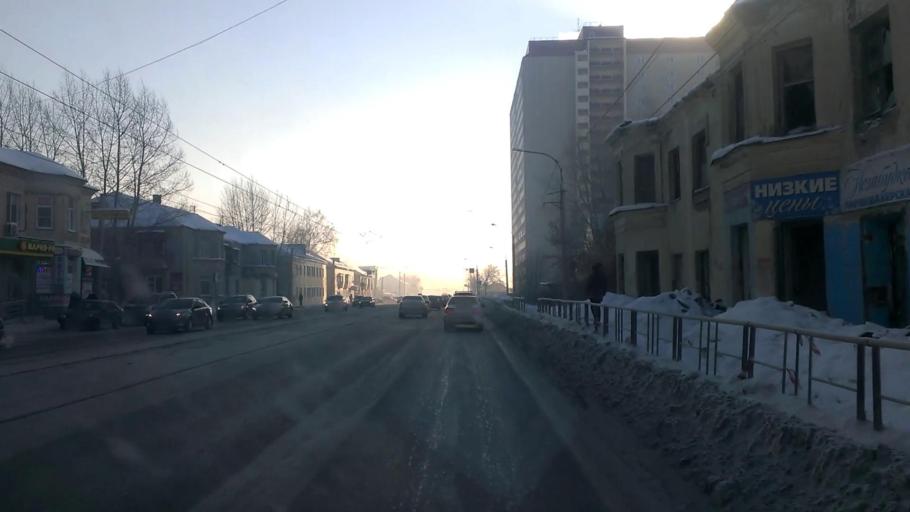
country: RU
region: Altai Krai
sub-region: Gorod Barnaulskiy
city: Barnaul
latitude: 53.3467
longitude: 83.7315
